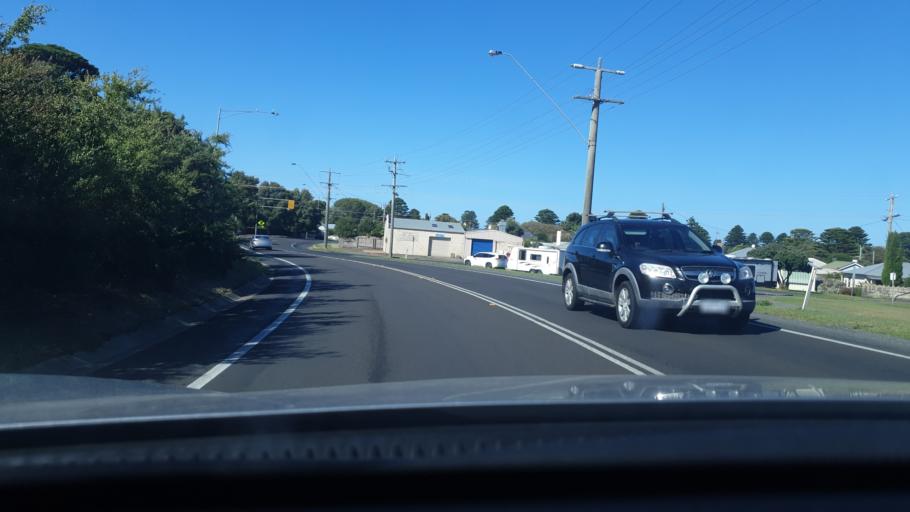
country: AU
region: Victoria
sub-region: Moyne
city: Port Fairy
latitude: -38.3850
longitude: 142.2250
